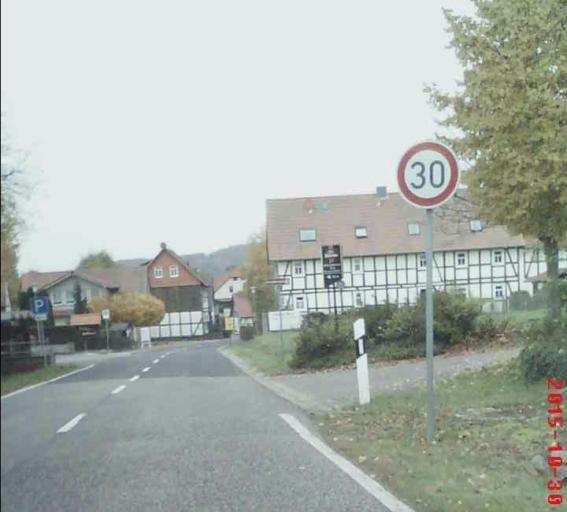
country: DE
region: Thuringia
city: Gerbershausen
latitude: 51.3345
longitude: 9.9879
